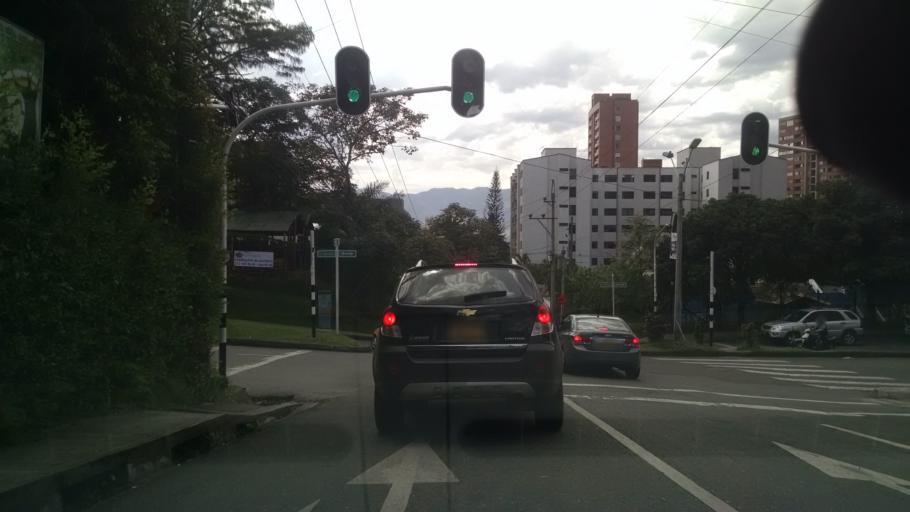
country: CO
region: Antioquia
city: Envigado
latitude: 6.2011
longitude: -75.5658
